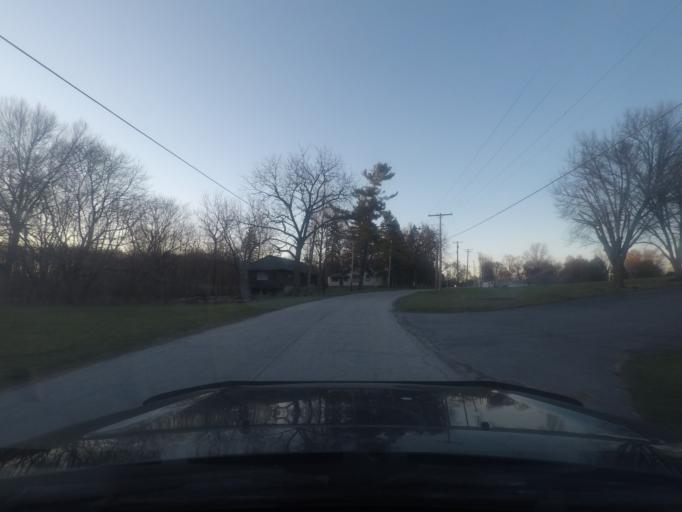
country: US
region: Indiana
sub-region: LaPorte County
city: Kingsford Heights
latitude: 41.5202
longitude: -86.7020
